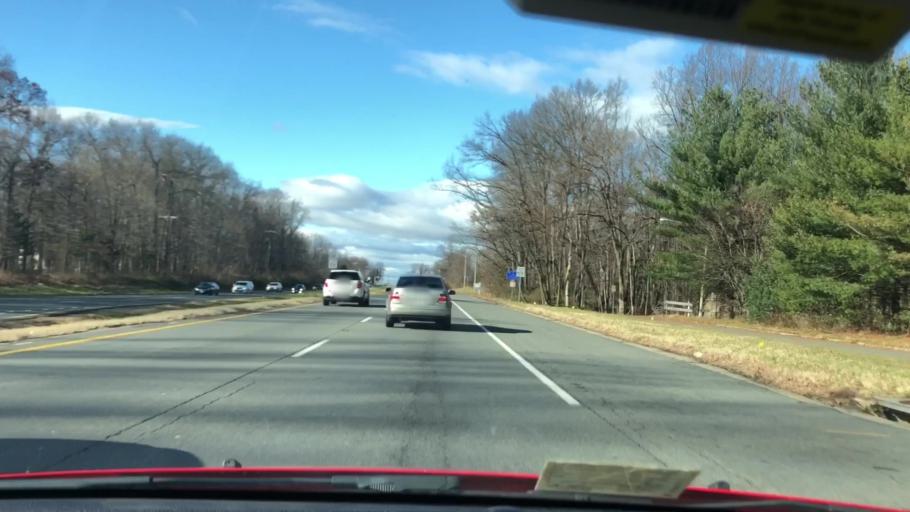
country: US
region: Virginia
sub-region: Fairfax County
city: Dranesville
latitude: 38.9952
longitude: -77.3369
